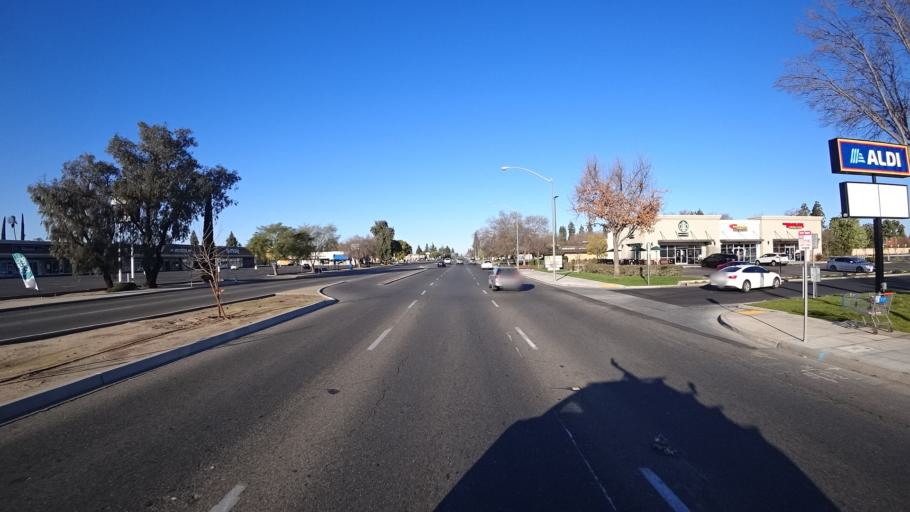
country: US
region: California
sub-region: Fresno County
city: Fresno
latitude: 36.8083
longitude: -119.8277
